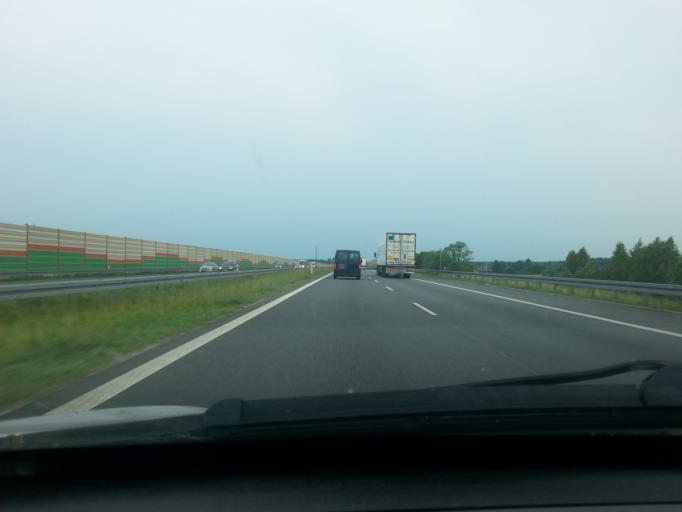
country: PL
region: Lodz Voivodeship
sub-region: Powiat skierniewicki
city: Bolimow
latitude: 52.0623
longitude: 20.1617
